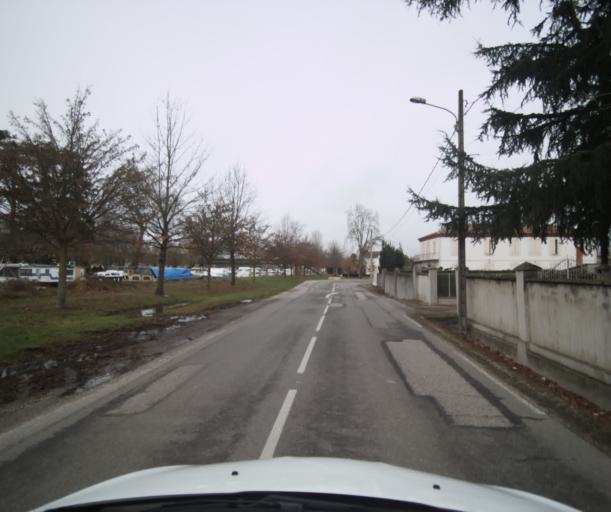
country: FR
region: Midi-Pyrenees
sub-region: Departement du Tarn-et-Garonne
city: Castelsarrasin
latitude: 44.0391
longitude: 1.1143
